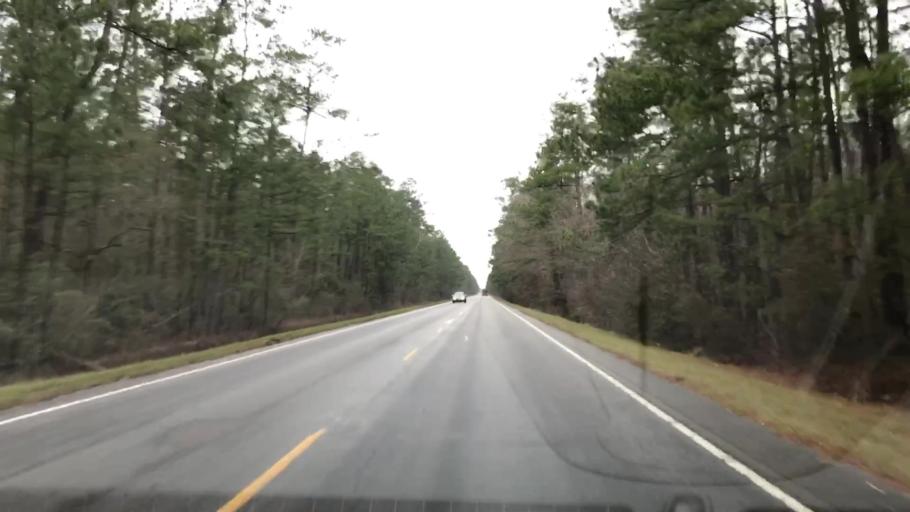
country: US
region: South Carolina
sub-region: Berkeley County
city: Saint Stephen
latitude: 33.2880
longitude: -79.8300
